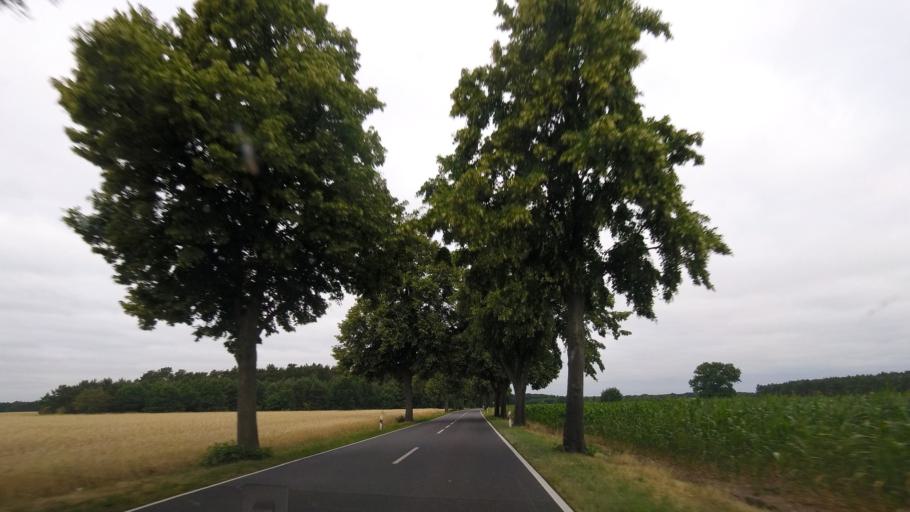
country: DE
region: Brandenburg
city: Treuenbrietzen
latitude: 52.1064
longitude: 12.8311
